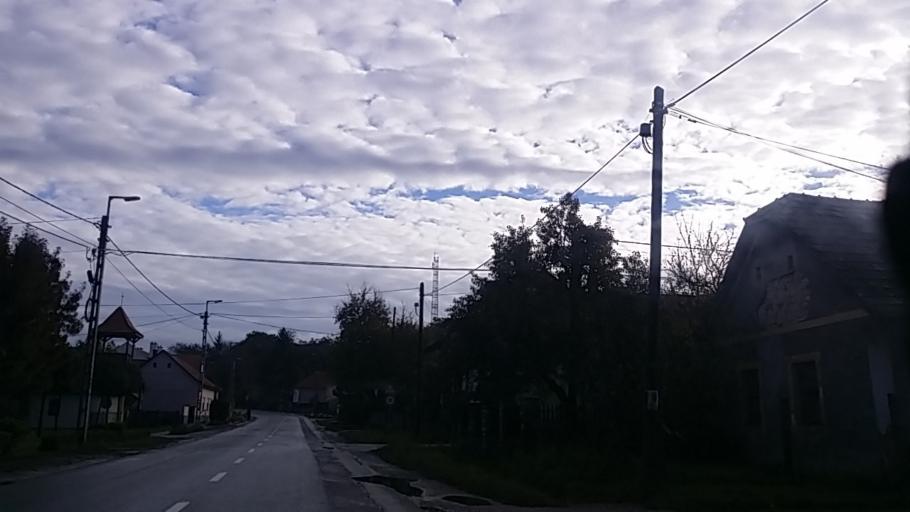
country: HU
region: Heves
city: Szilvasvarad
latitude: 48.1400
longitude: 20.4256
